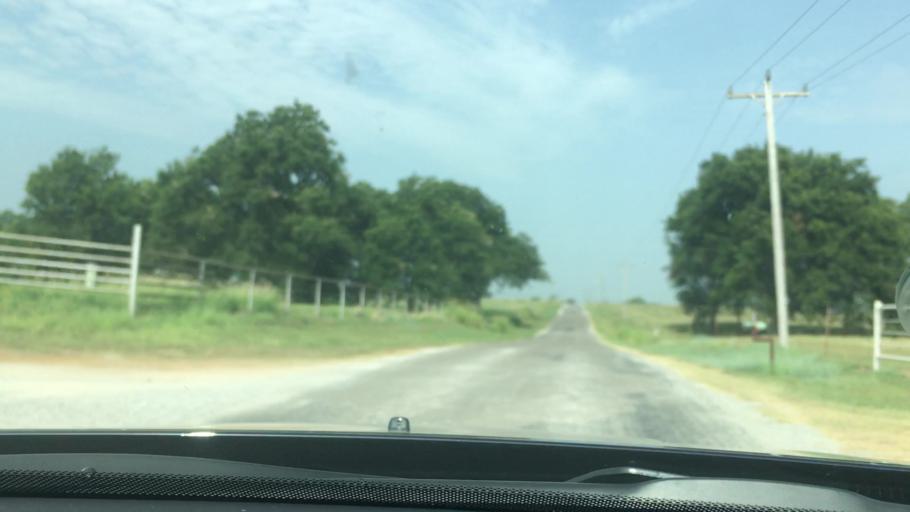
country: US
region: Oklahoma
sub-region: Garvin County
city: Pauls Valley
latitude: 34.7967
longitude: -97.1708
